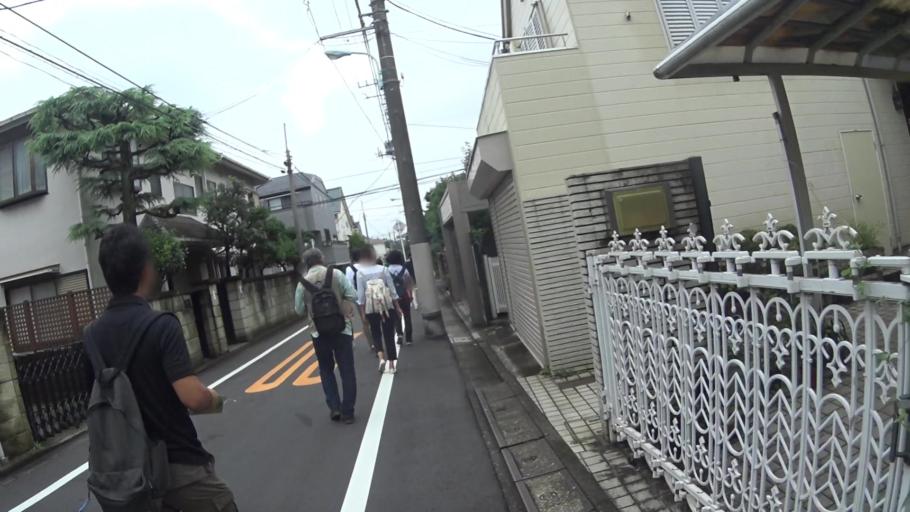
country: JP
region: Tokyo
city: Tokyo
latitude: 35.7342
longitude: 139.6811
